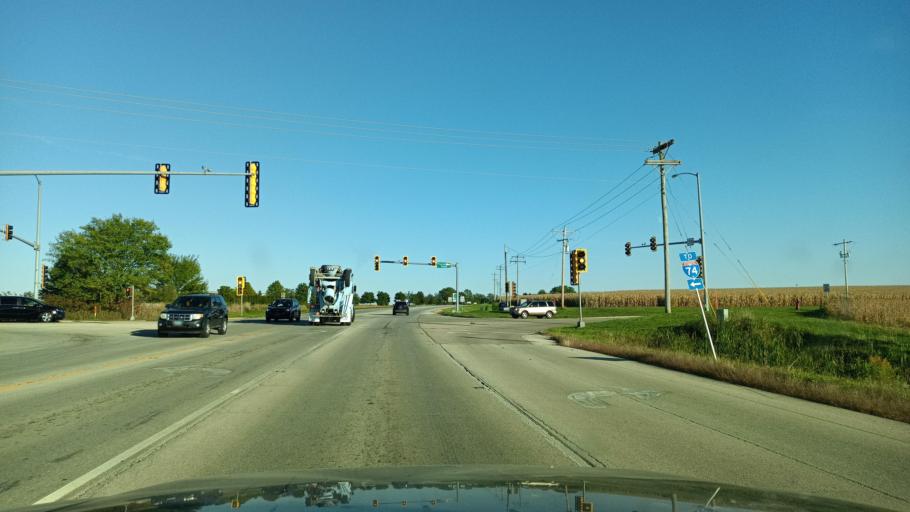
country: US
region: Illinois
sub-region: Champaign County
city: Lake of the Woods
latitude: 40.1845
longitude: -88.3660
